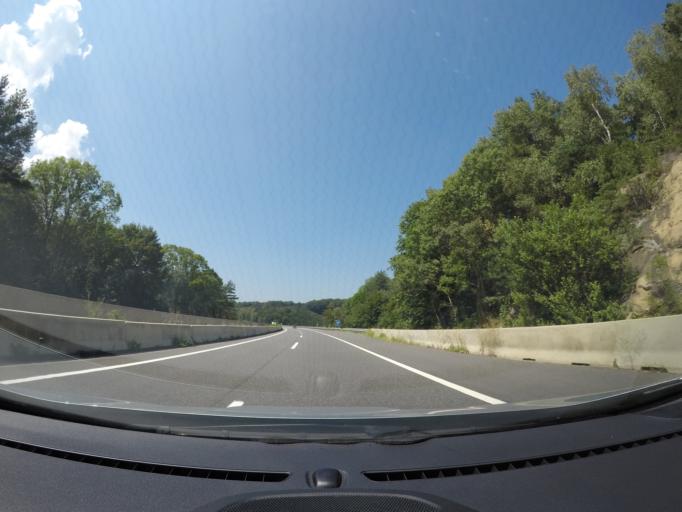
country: AT
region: Lower Austria
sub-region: Politischer Bezirk Sankt Polten
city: Eichgraben
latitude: 48.1626
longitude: 16.0001
